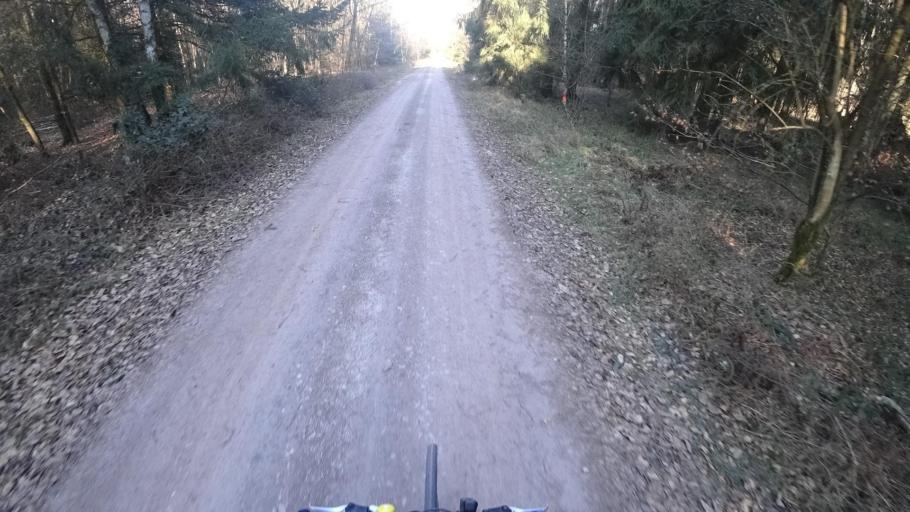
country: DE
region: Rheinland-Pfalz
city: Nortershausen
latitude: 50.2455
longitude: 7.5196
